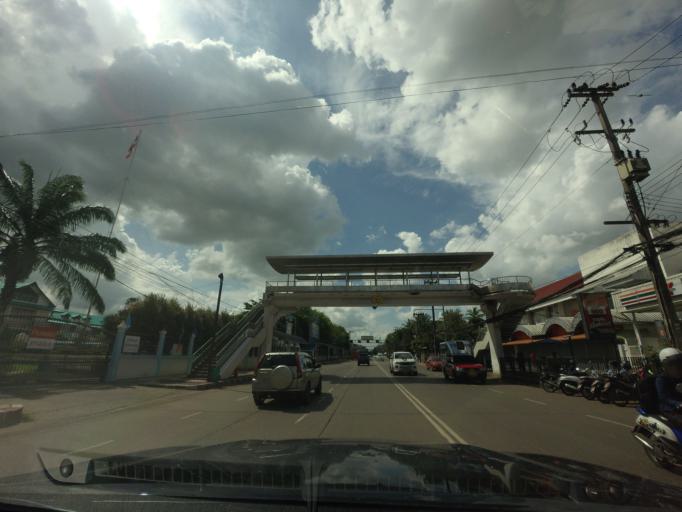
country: TH
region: Changwat Udon Thani
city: Udon Thani
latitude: 17.4089
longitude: 102.7796
